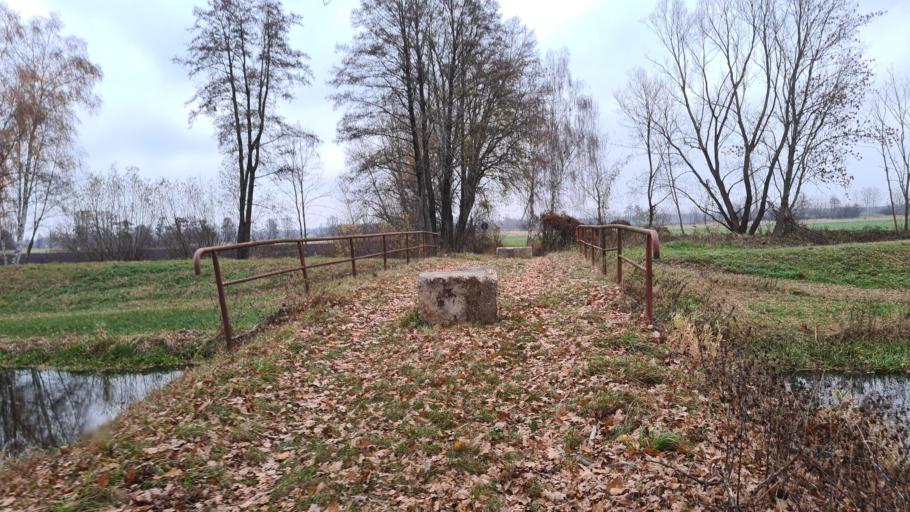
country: DE
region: Brandenburg
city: Hirschfeld
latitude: 51.4099
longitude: 13.6361
